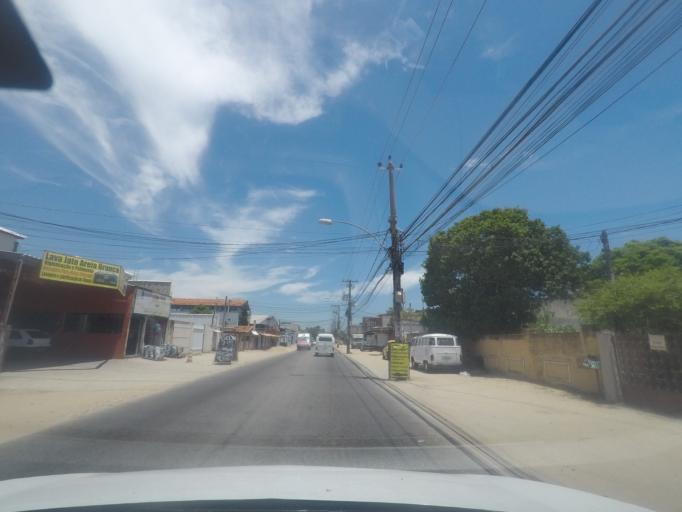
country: BR
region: Rio de Janeiro
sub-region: Itaguai
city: Itaguai
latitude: -22.9399
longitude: -43.6855
